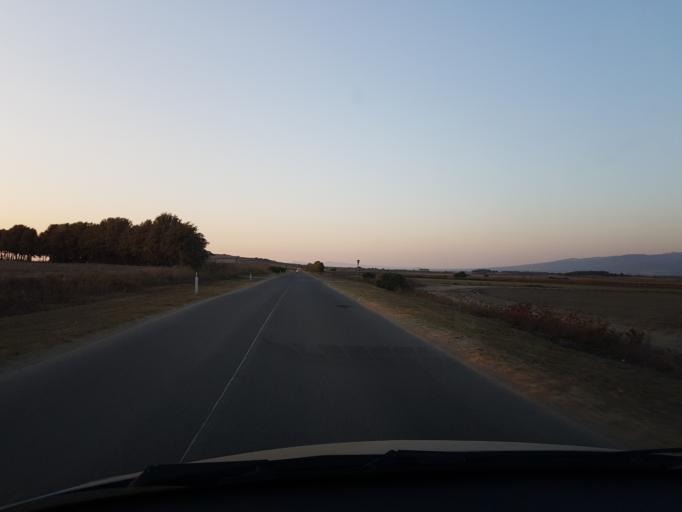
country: IT
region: Sardinia
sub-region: Provincia di Oristano
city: Nurachi
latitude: 39.9686
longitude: 8.4529
